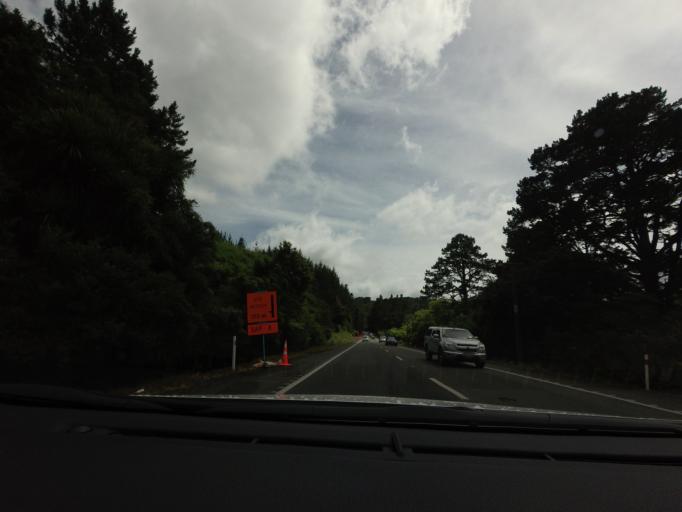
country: NZ
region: Auckland
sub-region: Auckland
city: Warkworth
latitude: -36.5066
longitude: 174.6706
